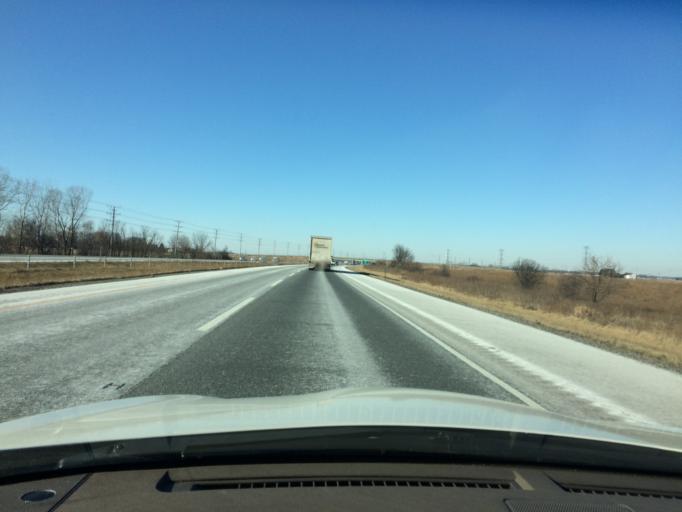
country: US
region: Illinois
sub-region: Kane County
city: Sugar Grove
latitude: 41.8014
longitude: -88.4203
